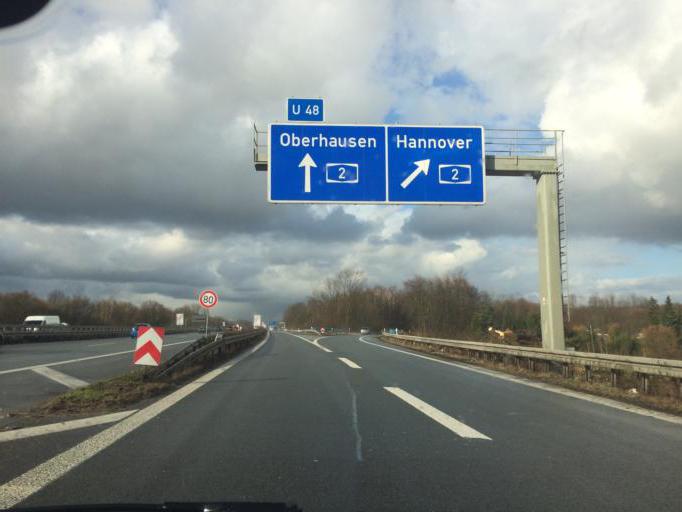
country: DE
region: North Rhine-Westphalia
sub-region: Regierungsbezirk Munster
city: Recklinghausen
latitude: 51.5800
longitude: 7.1905
